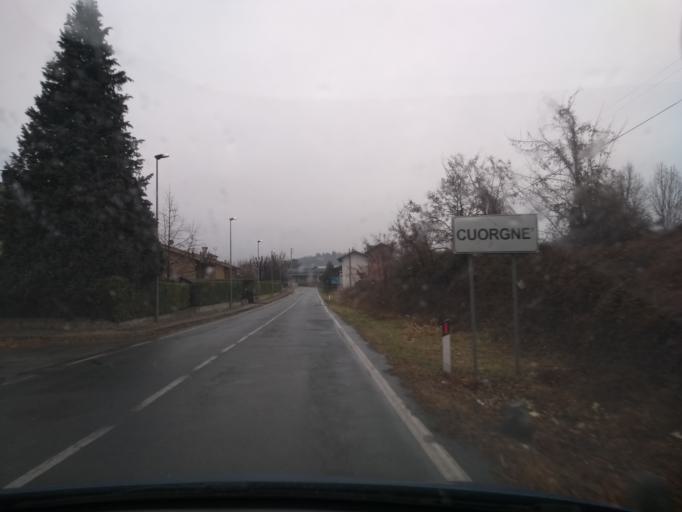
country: IT
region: Piedmont
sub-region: Provincia di Torino
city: Valperga
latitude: 45.3824
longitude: 7.6600
